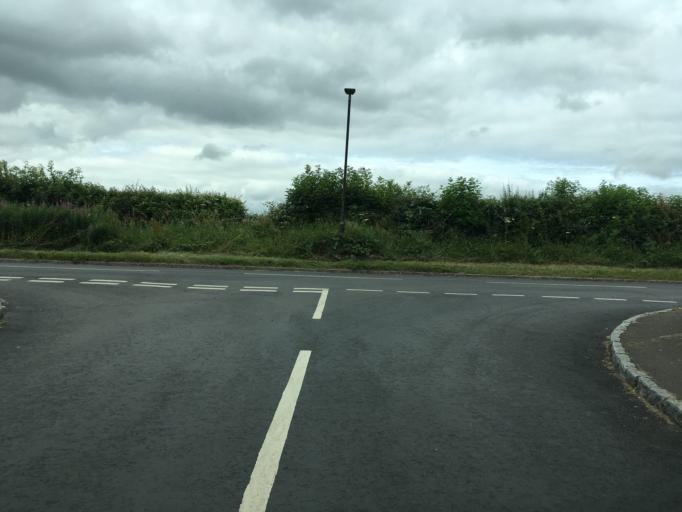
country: GB
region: England
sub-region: Gloucestershire
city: Bourton on the Water
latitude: 51.8775
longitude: -1.7060
